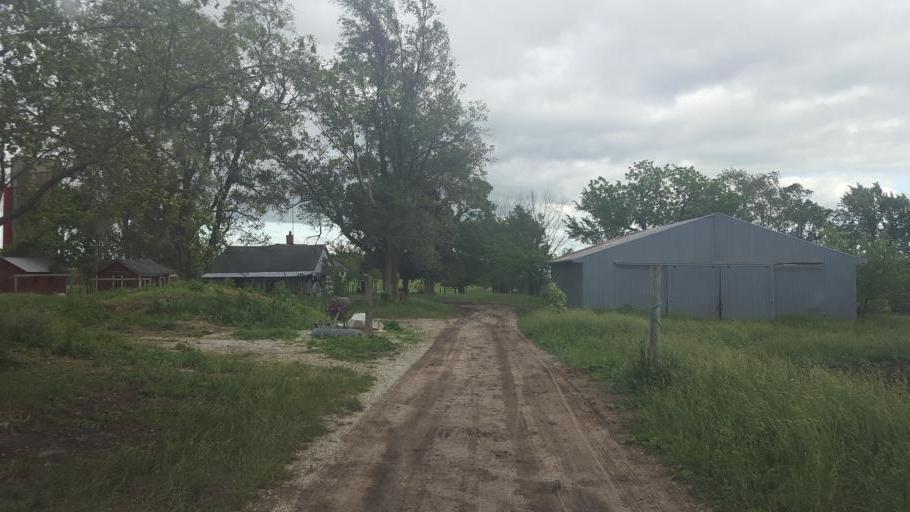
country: US
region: Missouri
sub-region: Mercer County
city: Princeton
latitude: 40.2554
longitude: -93.6723
